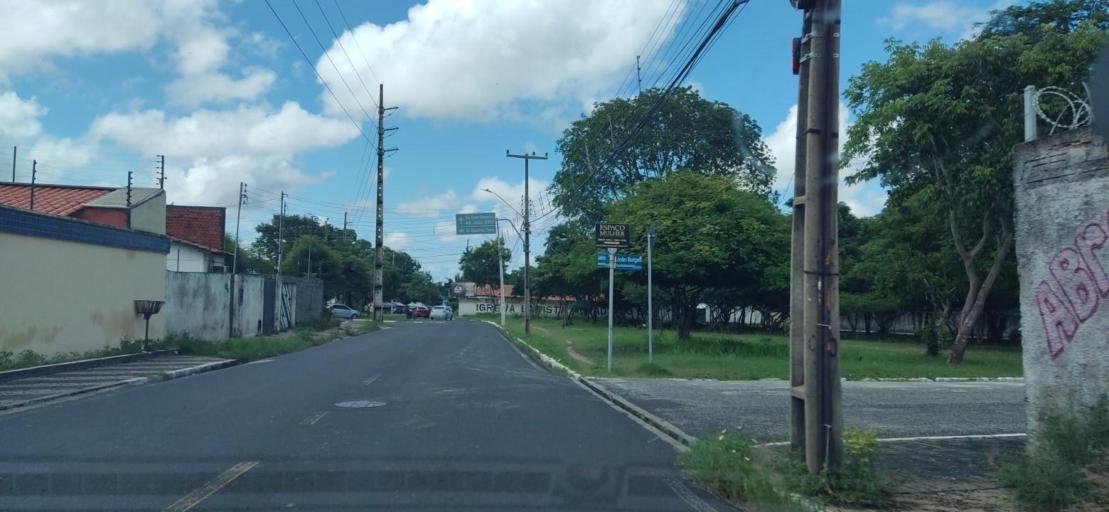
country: BR
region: Piaui
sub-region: Teresina
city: Teresina
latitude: -5.0693
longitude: -42.7605
